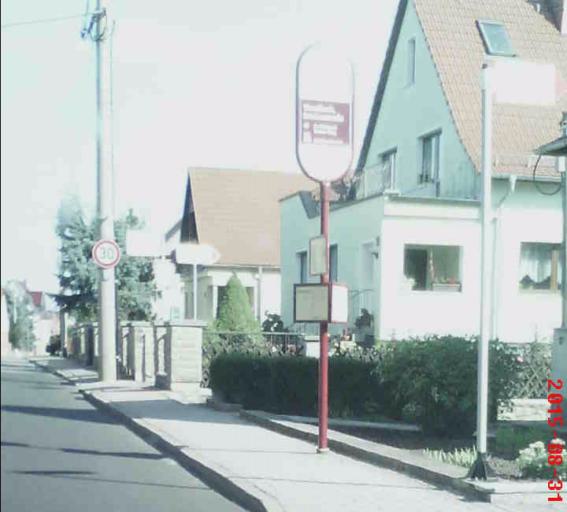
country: DE
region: Thuringia
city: Monchenholzhausen
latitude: 50.9961
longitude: 11.1441
